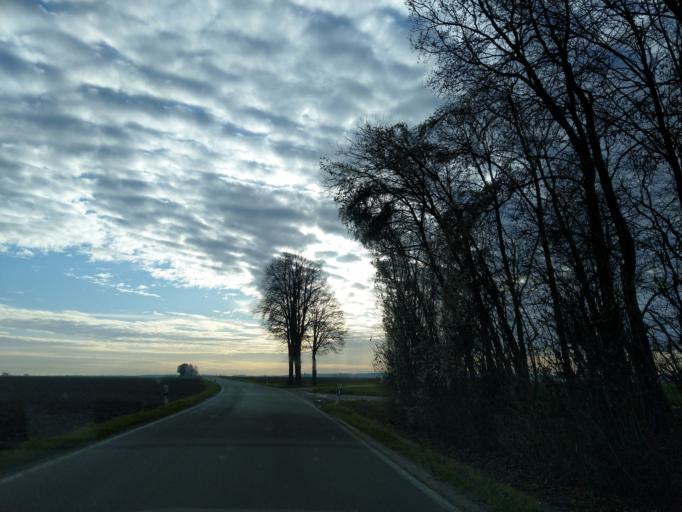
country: DE
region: Bavaria
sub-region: Lower Bavaria
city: Aholming
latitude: 48.7144
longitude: 12.9081
